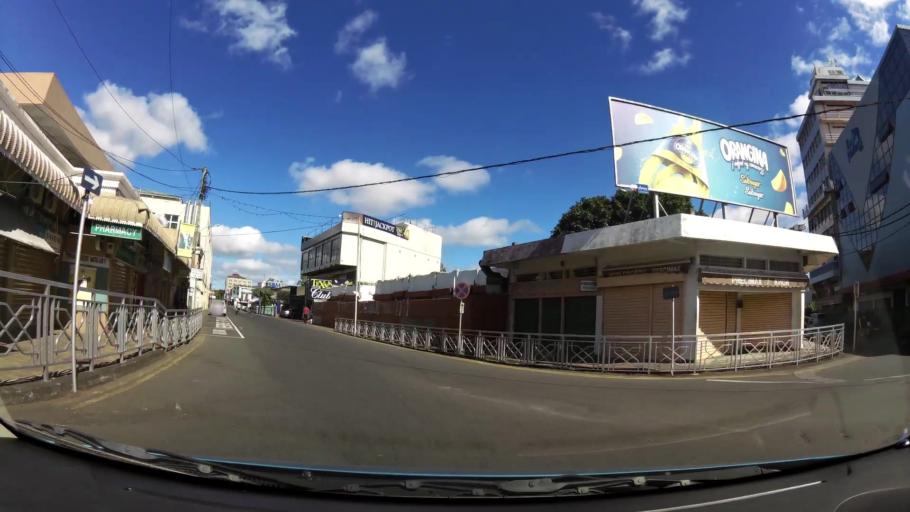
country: MU
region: Plaines Wilhems
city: Vacoas
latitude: -20.2959
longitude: 57.4930
